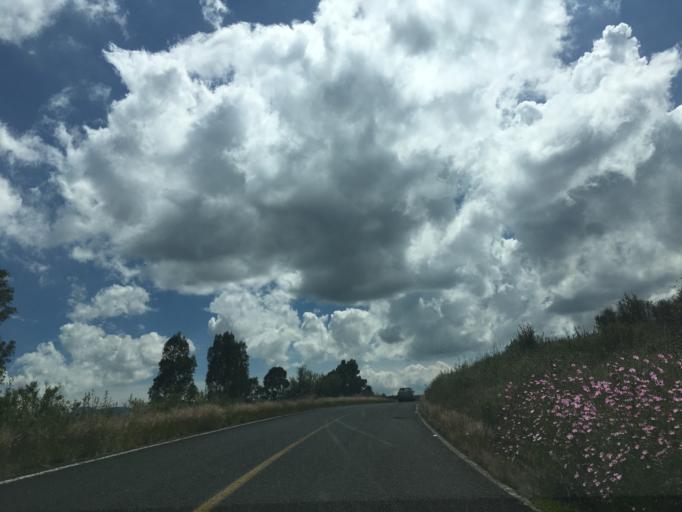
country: MX
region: Michoacan
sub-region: Morelia
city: Cuto de la Esperanza
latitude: 19.7802
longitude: -101.4018
